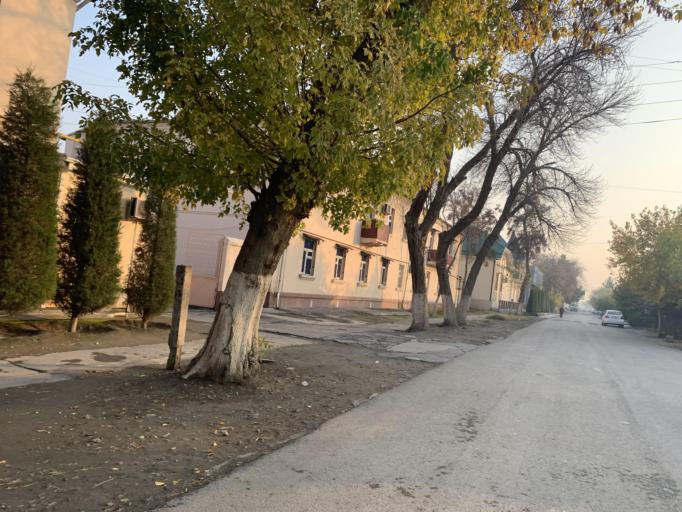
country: UZ
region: Fergana
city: Qo`qon
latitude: 40.5217
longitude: 70.9381
